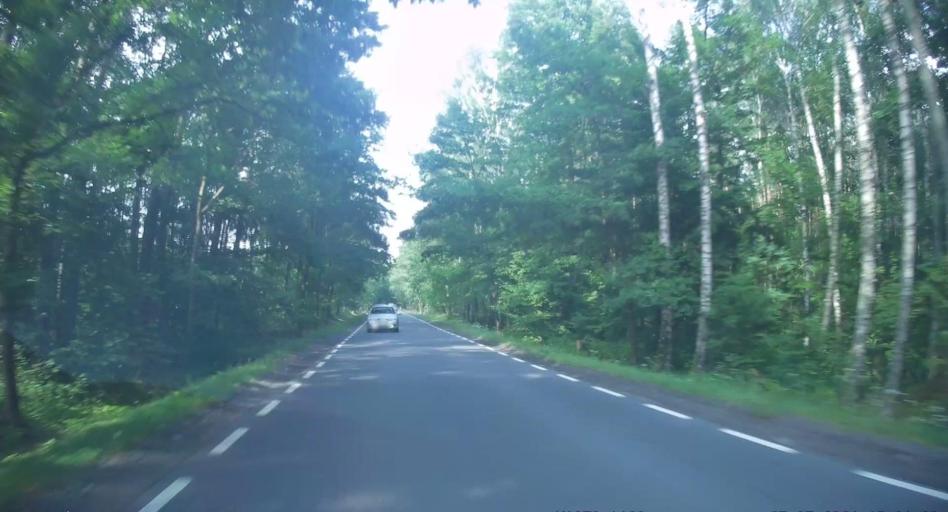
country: PL
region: Lodz Voivodeship
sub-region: Powiat tomaszowski
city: Rzeczyca
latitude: 51.5704
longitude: 20.2760
